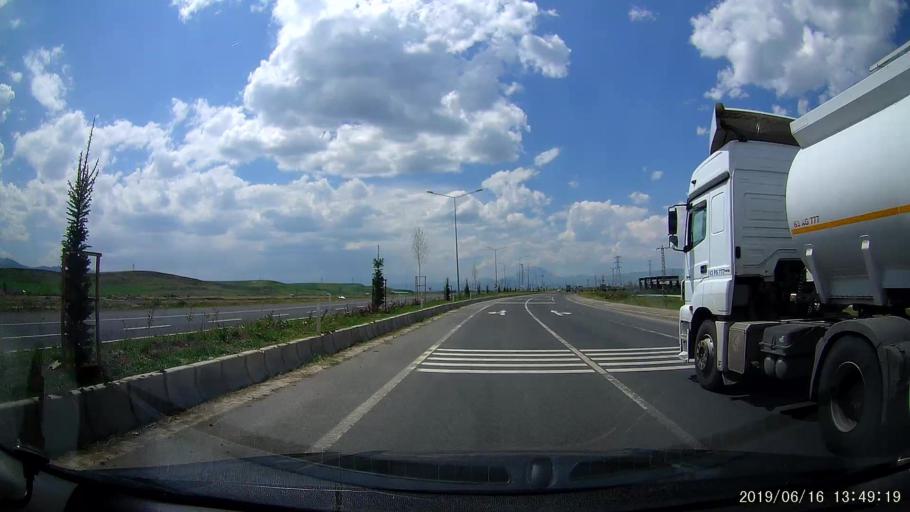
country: TR
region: Agri
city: Agri
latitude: 39.7163
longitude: 42.9923
